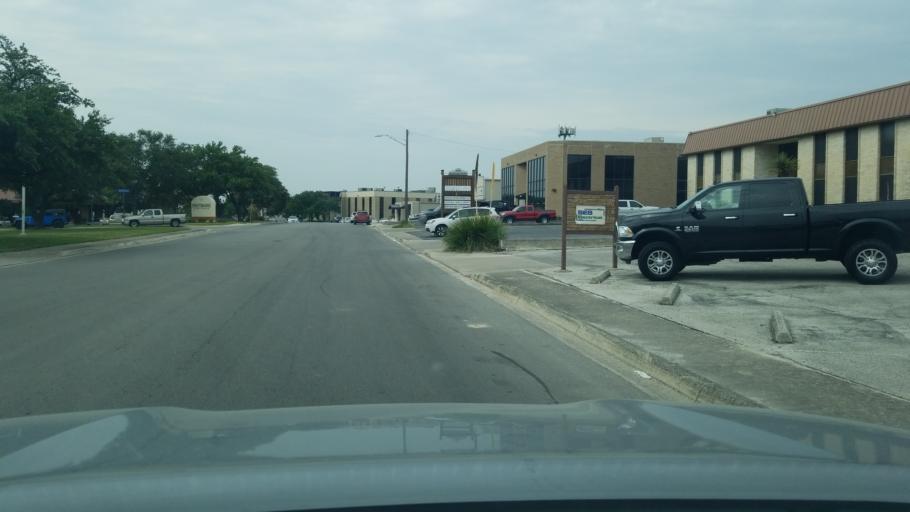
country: US
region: Texas
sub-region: Bexar County
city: Castle Hills
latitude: 29.5396
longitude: -98.4909
